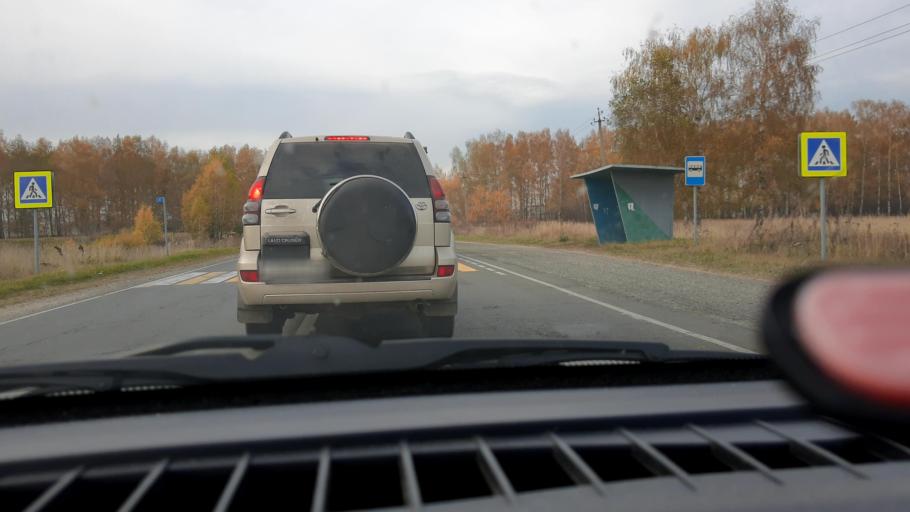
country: RU
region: Nizjnij Novgorod
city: Gorodets
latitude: 56.6299
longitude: 43.5393
